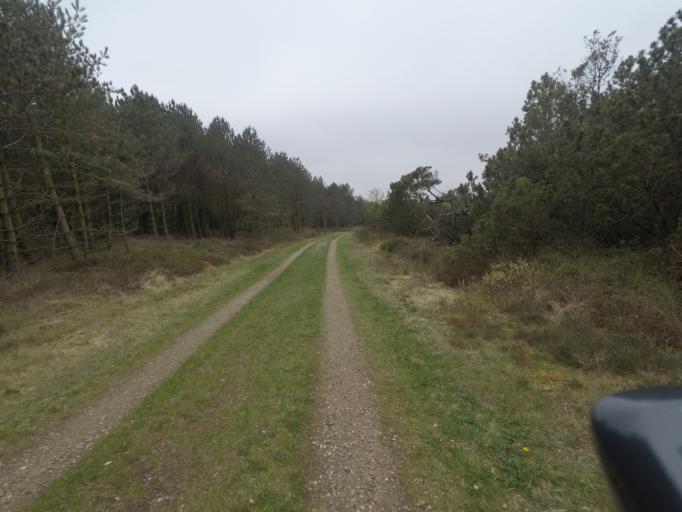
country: DE
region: Schleswig-Holstein
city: List
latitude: 55.1233
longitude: 8.5366
